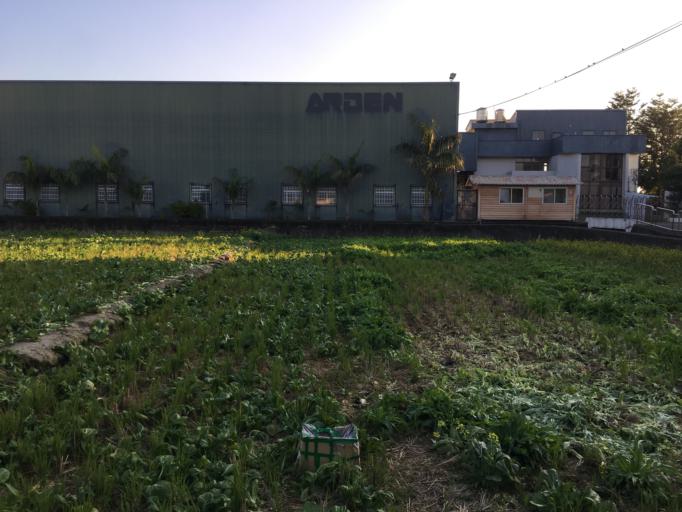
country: TW
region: Taiwan
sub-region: Taichung City
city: Taichung
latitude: 24.1179
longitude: 120.6241
